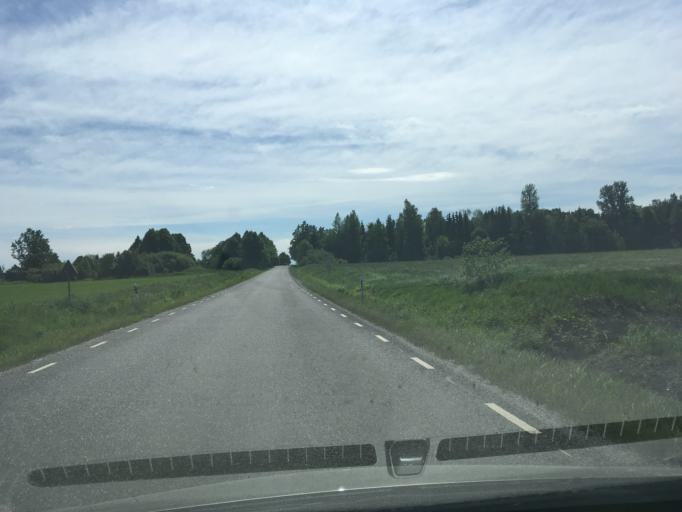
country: EE
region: Paernumaa
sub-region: Audru vald
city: Audru
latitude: 58.4423
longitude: 24.3931
